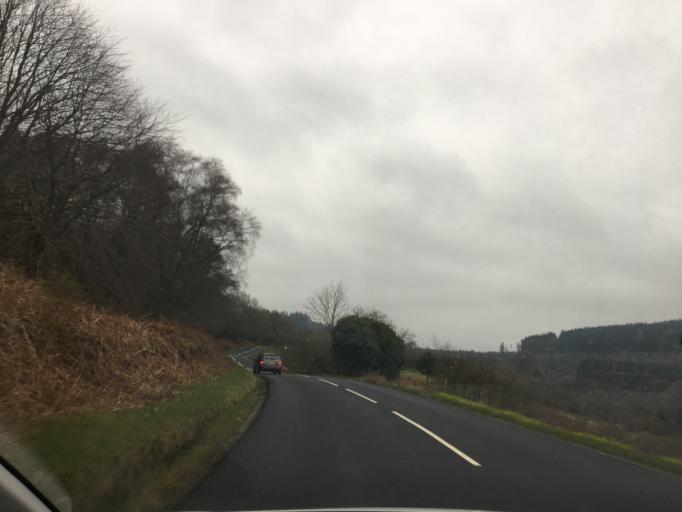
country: GB
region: Scotland
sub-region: North Ayrshire
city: Lamlash
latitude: 55.5467
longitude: -5.1349
